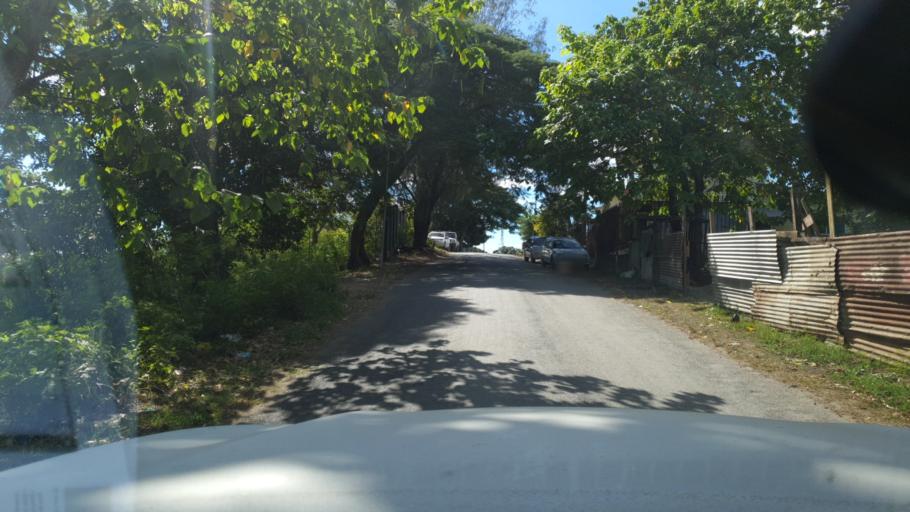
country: SB
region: Guadalcanal
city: Honiara
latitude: -9.4349
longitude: 159.9535
